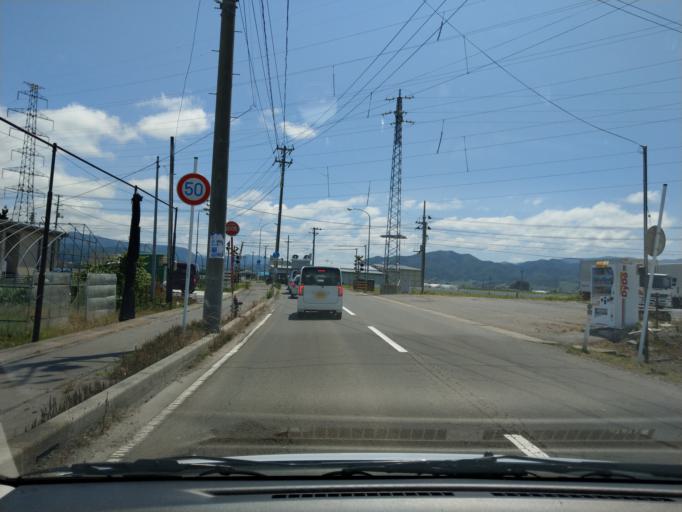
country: JP
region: Aomori
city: Kuroishi
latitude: 40.5825
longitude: 140.5509
